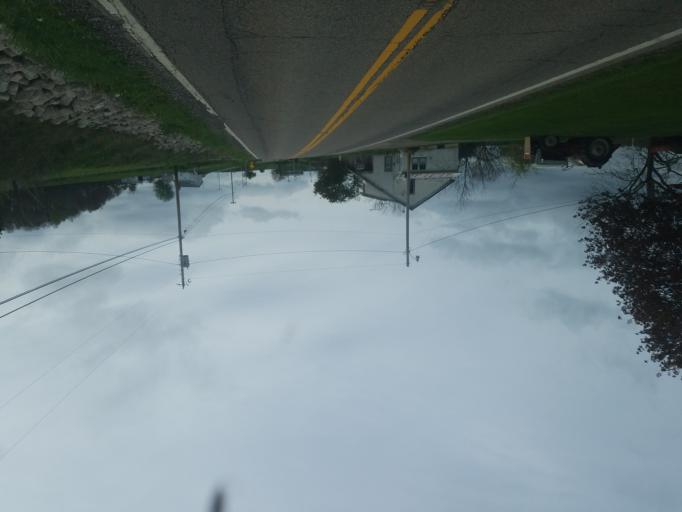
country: US
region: Ohio
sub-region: Wayne County
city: Shreve
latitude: 40.6019
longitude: -82.1082
